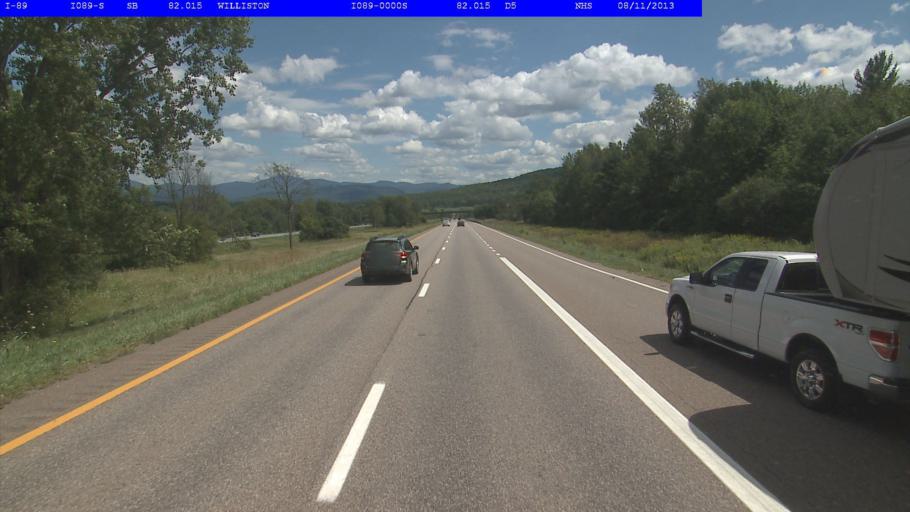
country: US
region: Vermont
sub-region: Chittenden County
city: Williston
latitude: 44.4348
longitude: -73.0766
